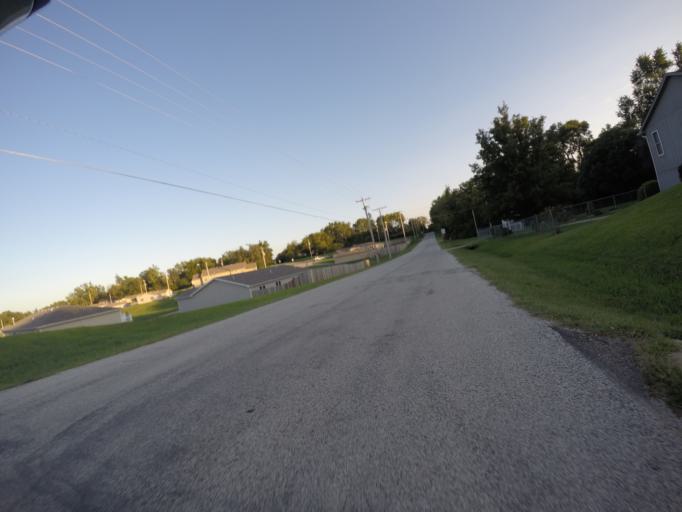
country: US
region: Kansas
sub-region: Riley County
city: Ogden
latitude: 39.1203
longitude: -96.7115
